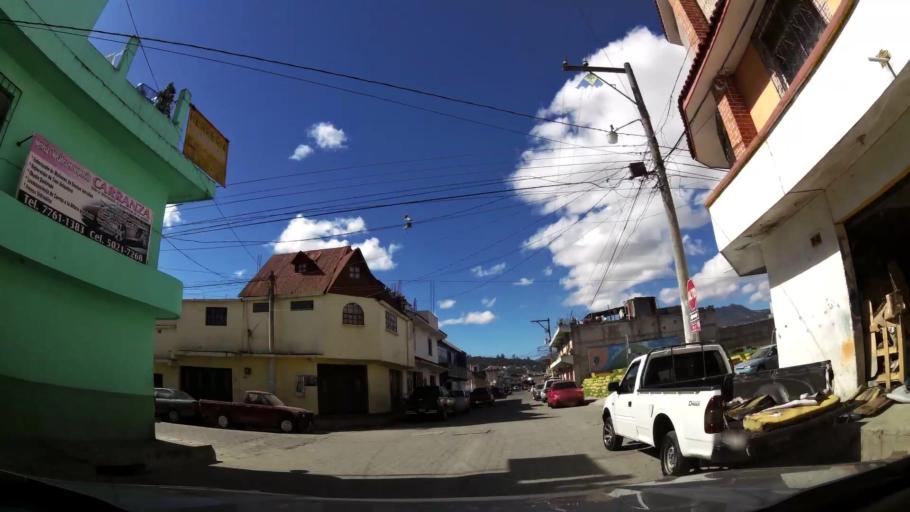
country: GT
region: Quetzaltenango
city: Quetzaltenango
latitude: 14.8414
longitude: -91.5067
